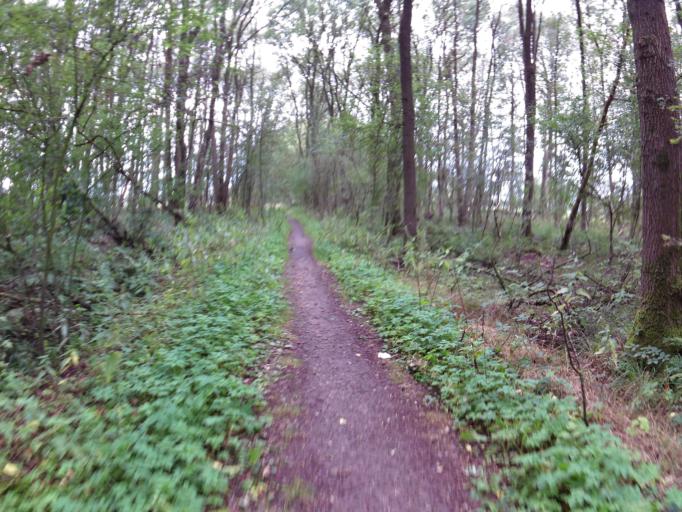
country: NL
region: Gelderland
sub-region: Berkelland
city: Eibergen
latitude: 52.0406
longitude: 6.6885
